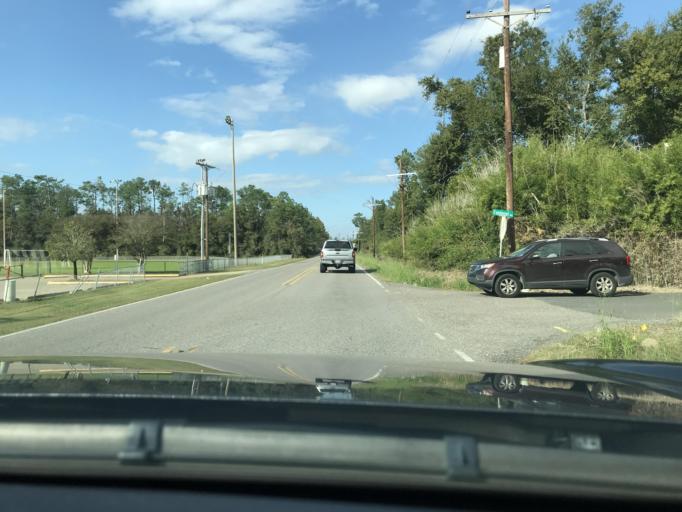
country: US
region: Louisiana
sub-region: Calcasieu Parish
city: Westlake
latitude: 30.2823
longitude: -93.2582
